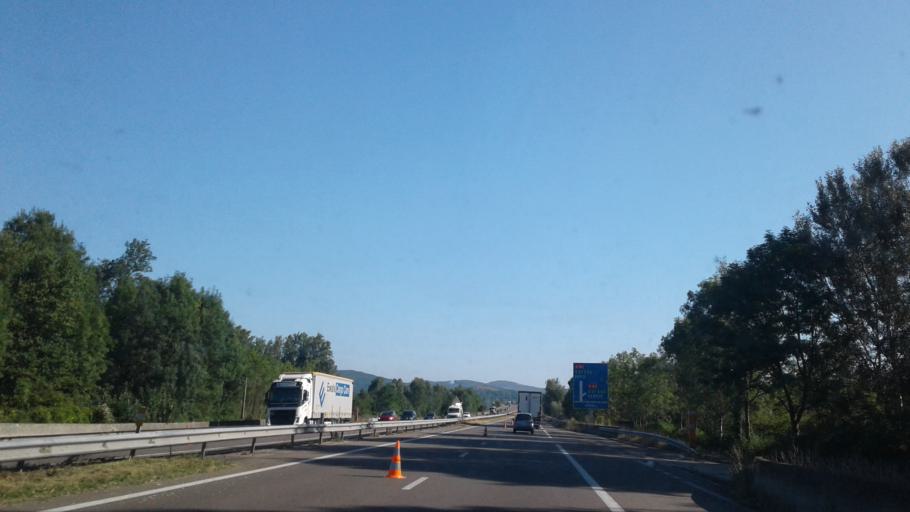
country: FR
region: Rhone-Alpes
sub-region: Departement de l'Ain
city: Saint-Martin-du-Mont
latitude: 46.0497
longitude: 5.3264
